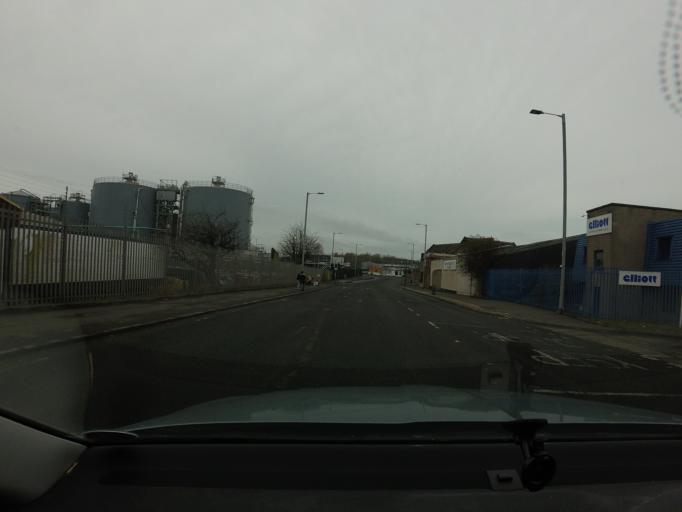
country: GB
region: Scotland
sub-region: South Lanarkshire
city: Rutherglen
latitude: 55.8355
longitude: -4.2439
